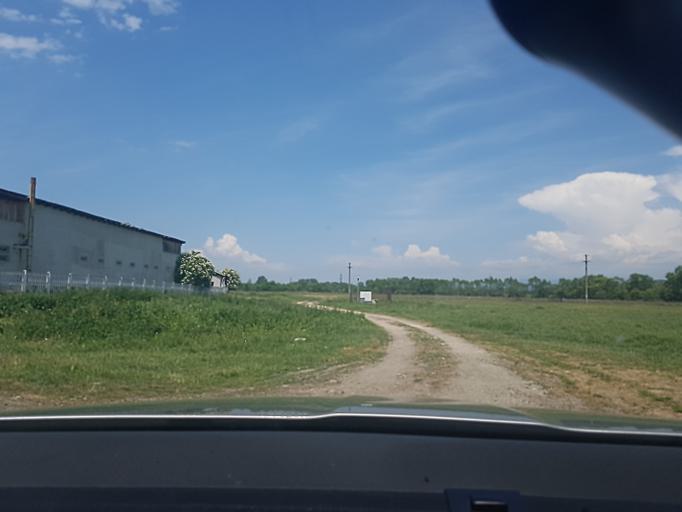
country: RO
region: Hunedoara
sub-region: Comuna Calan
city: Calan
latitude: 45.7441
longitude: 23.0078
